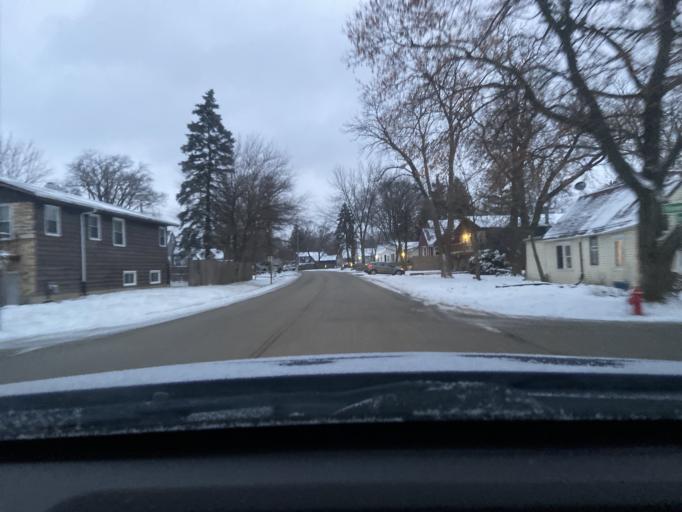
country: US
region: Illinois
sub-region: Lake County
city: Round Lake Park
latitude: 42.3499
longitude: -88.0800
